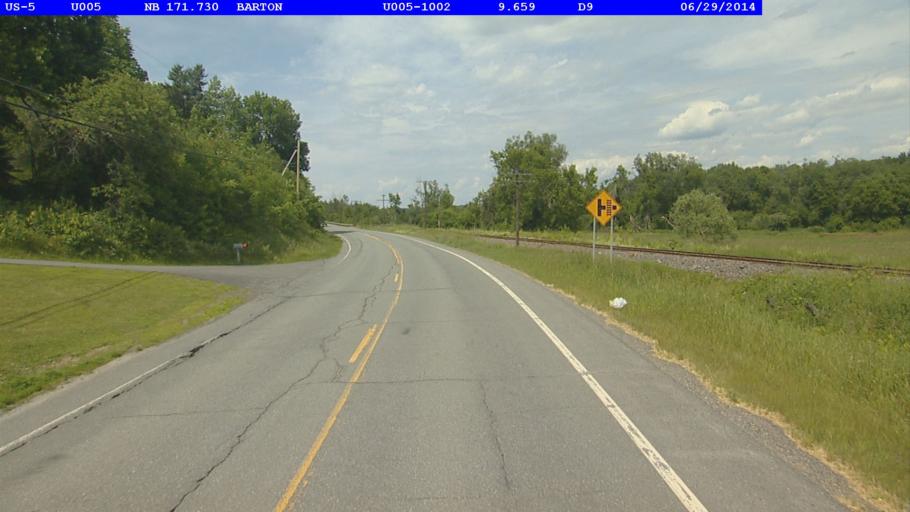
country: US
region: Vermont
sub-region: Orleans County
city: Newport
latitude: 44.7962
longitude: -72.2110
